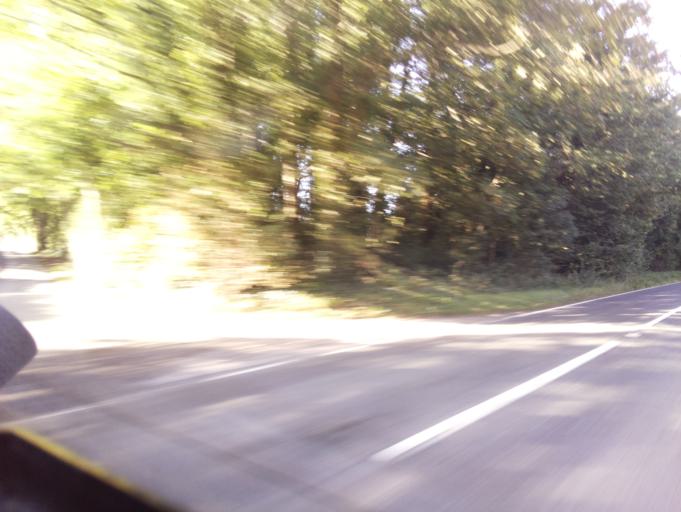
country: GB
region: England
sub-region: Hampshire
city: Swanmore
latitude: 50.9954
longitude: -1.1184
